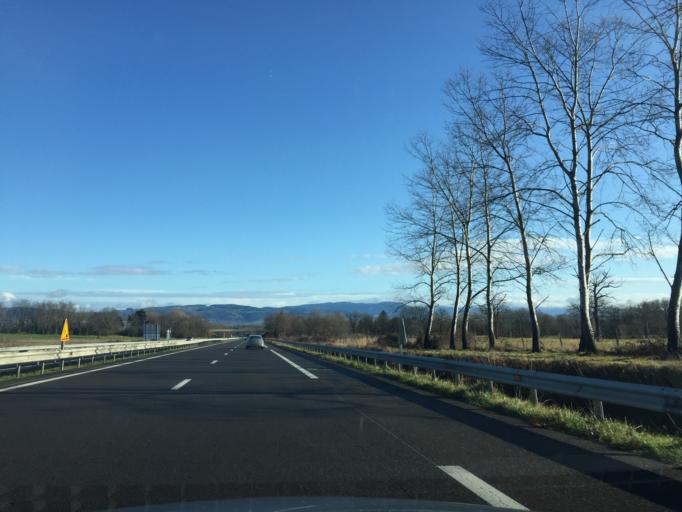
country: FR
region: Auvergne
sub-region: Departement du Puy-de-Dome
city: Orleat
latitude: 45.8503
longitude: 3.4198
